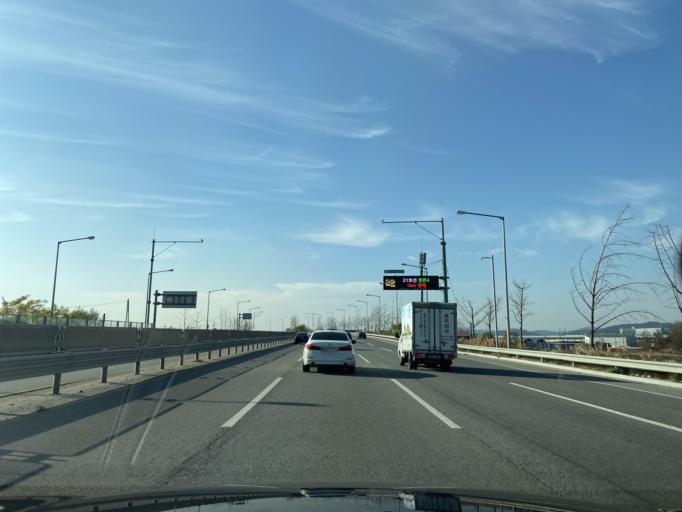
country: KR
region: Chungcheongnam-do
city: Asan
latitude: 36.7787
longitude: 127.0689
